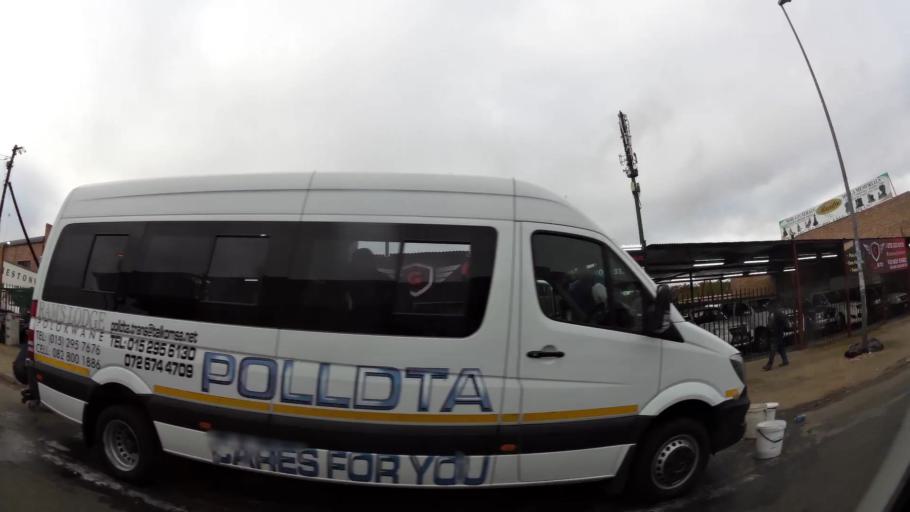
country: ZA
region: Limpopo
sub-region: Capricorn District Municipality
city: Polokwane
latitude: -23.9058
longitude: 29.4465
